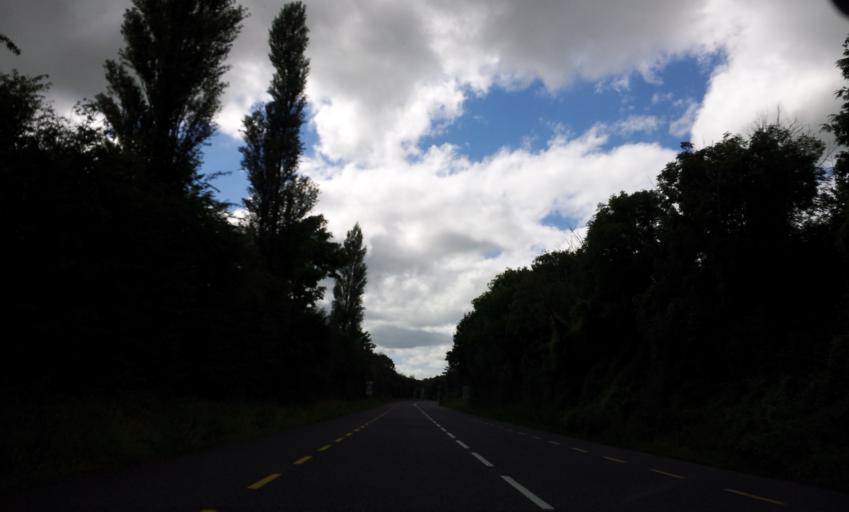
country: IE
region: Munster
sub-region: County Cork
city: Killumney
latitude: 51.8727
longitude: -8.7243
